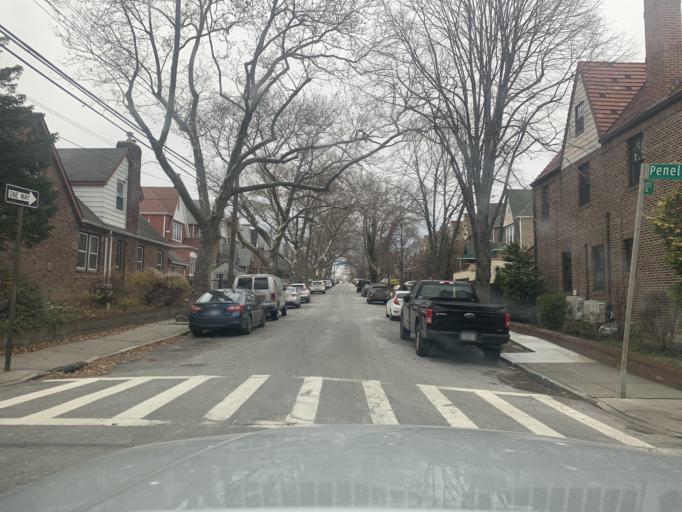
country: US
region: New York
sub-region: Queens County
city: Borough of Queens
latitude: 40.7205
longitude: -73.8723
